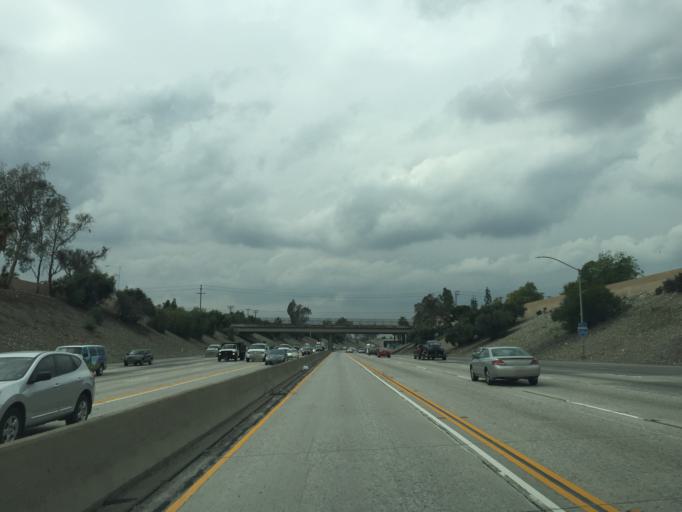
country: US
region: California
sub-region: Los Angeles County
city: Azusa
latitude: 34.1282
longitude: -117.9194
